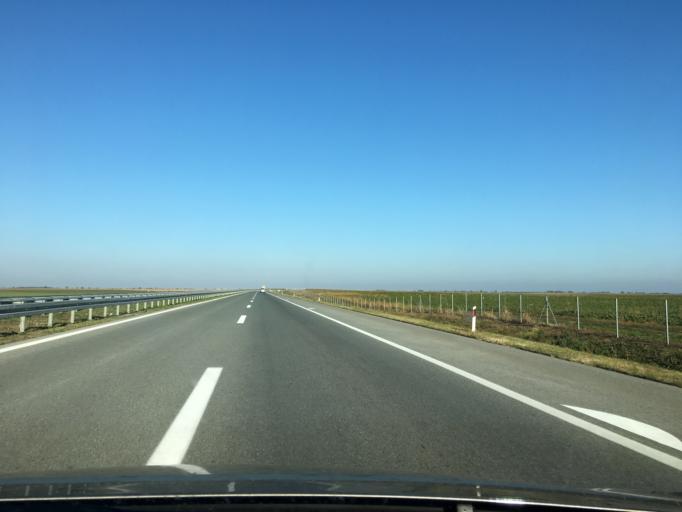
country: RS
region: Autonomna Pokrajina Vojvodina
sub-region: Severnobacki Okrug
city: Mali Igos
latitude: 45.7168
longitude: 19.7116
